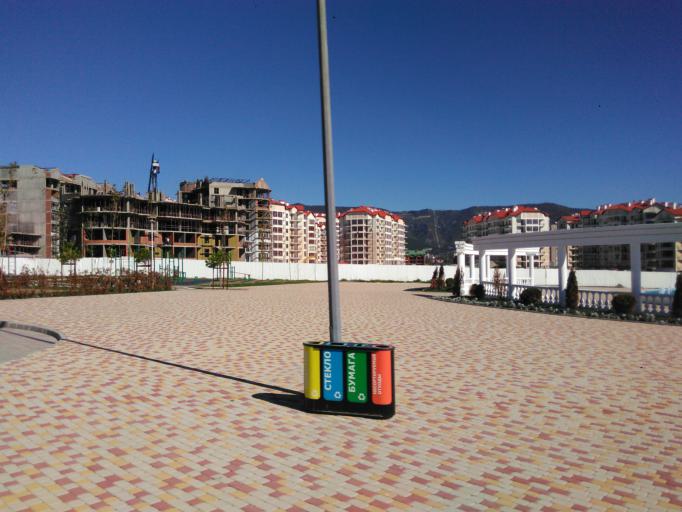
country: RU
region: Krasnodarskiy
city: Gelendzhik
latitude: 44.5481
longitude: 38.0563
